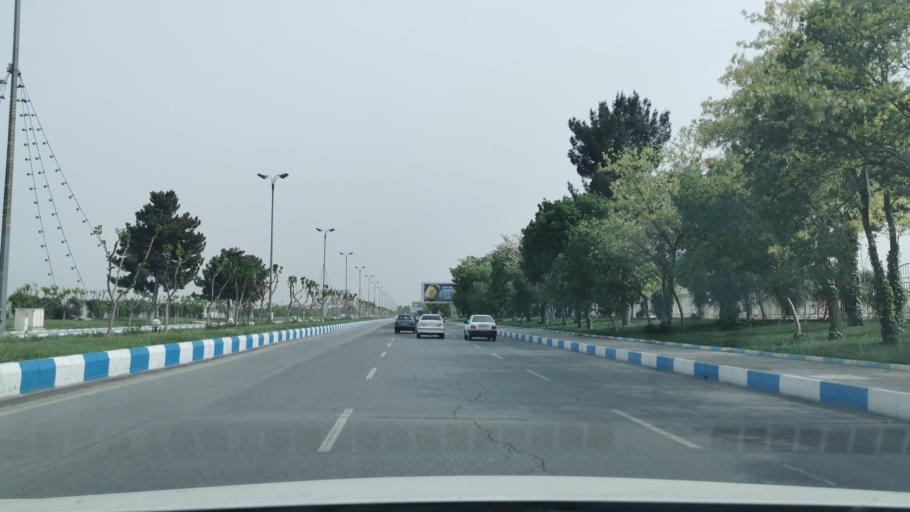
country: IR
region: Razavi Khorasan
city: Mashhad
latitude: 36.2399
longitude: 59.6267
